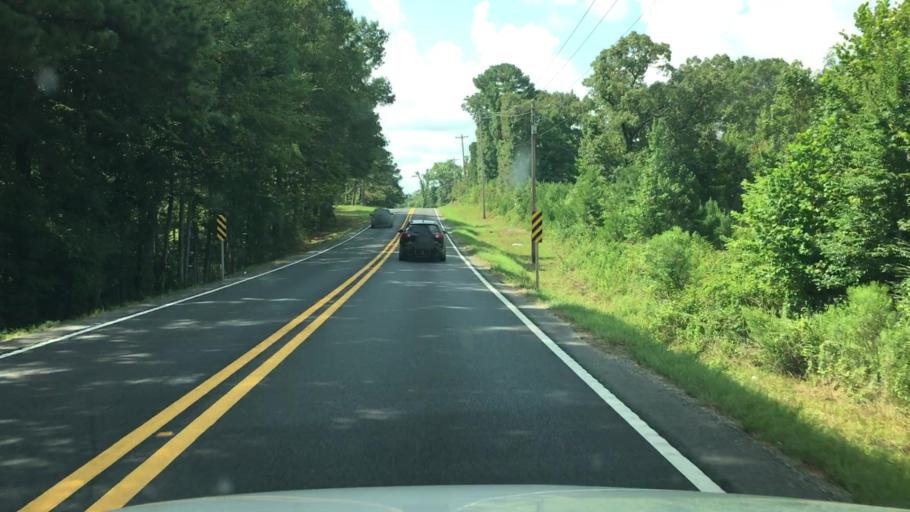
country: US
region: Arkansas
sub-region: Garland County
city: Lake Hamilton
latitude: 34.2882
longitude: -93.1635
